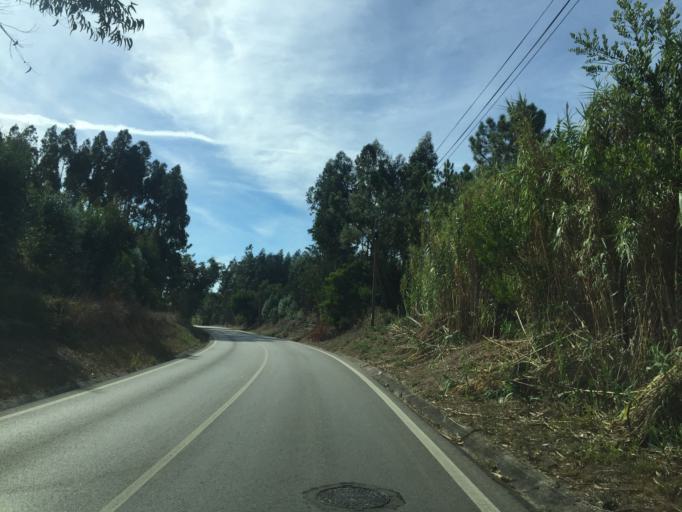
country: PT
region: Coimbra
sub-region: Figueira da Foz
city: Lavos
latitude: 40.0816
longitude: -8.8236
